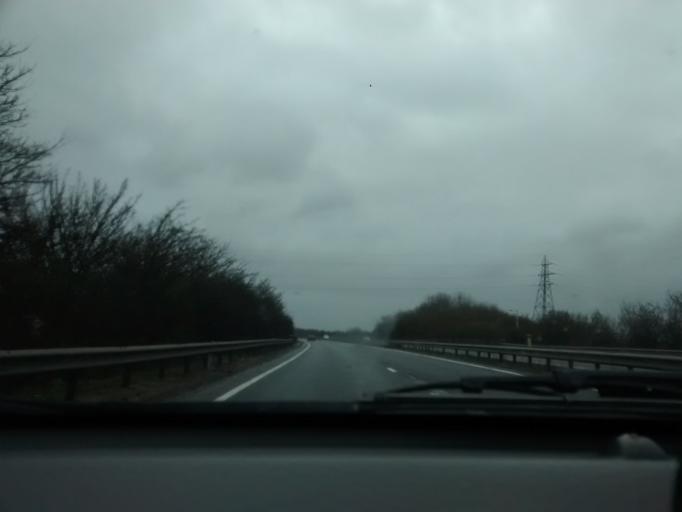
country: GB
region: England
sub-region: Suffolk
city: Stowmarket
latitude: 52.1871
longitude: 1.0222
